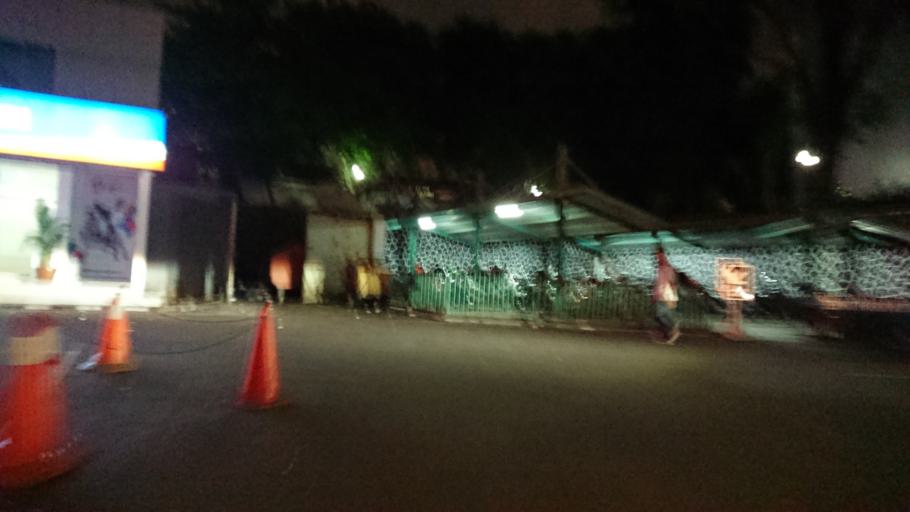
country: ID
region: Jakarta Raya
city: Jakarta
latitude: -6.2139
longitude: 106.7987
